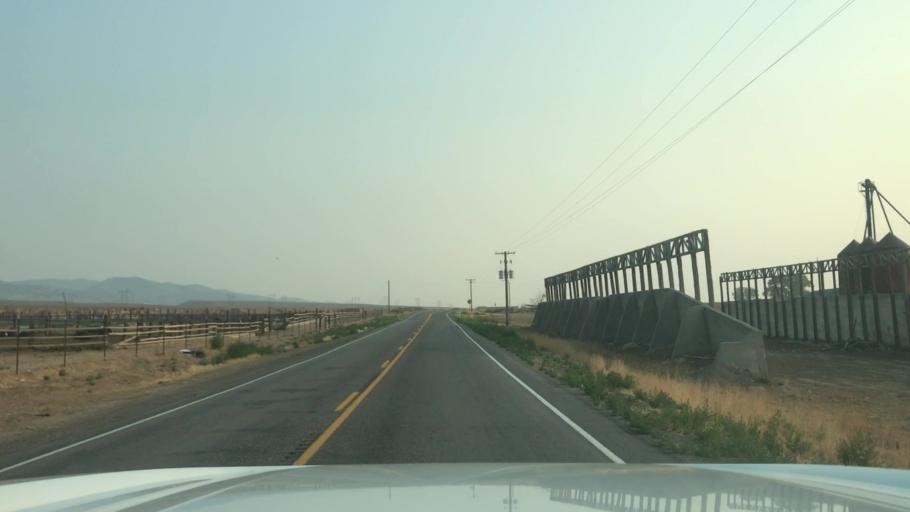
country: US
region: Utah
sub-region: Sevier County
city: Aurora
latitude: 38.9448
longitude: -111.9346
